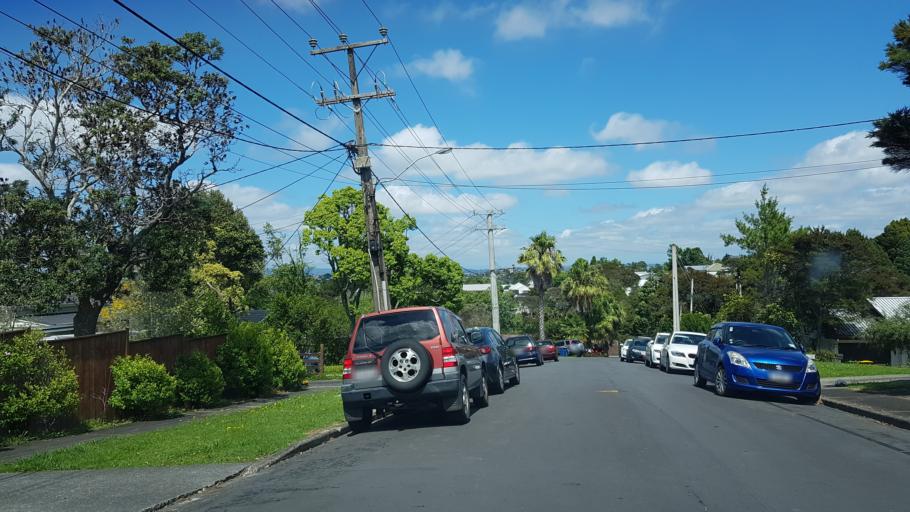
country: NZ
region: Auckland
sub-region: Auckland
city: North Shore
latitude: -36.7908
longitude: 174.7165
